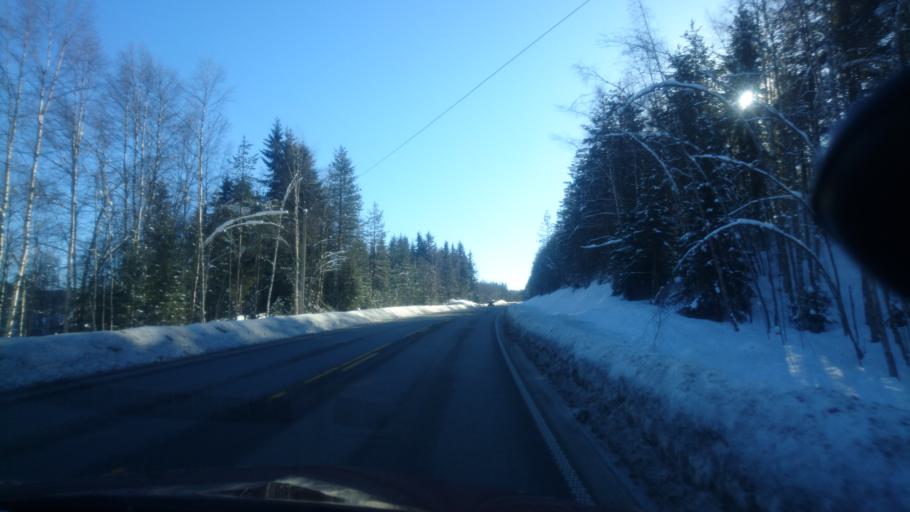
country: NO
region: Hedmark
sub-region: Trysil
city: Innbygda
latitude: 61.2682
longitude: 12.3052
